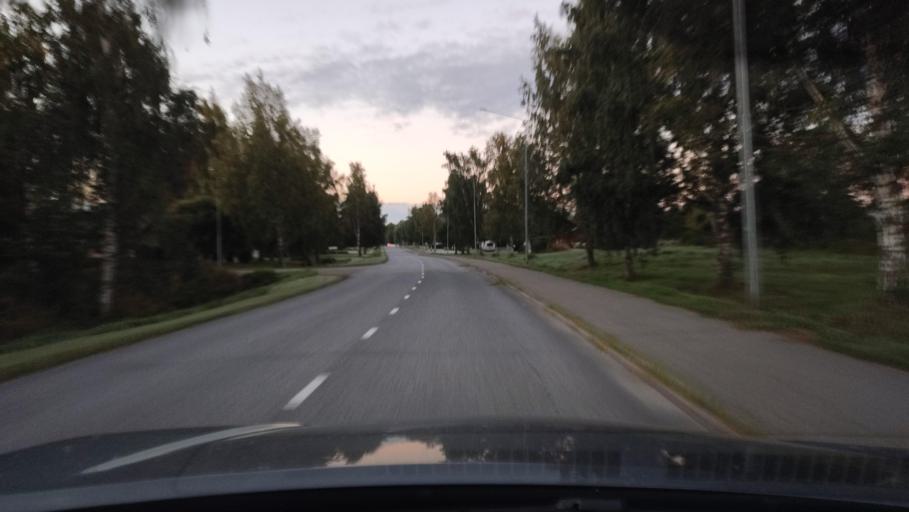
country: FI
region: Ostrobothnia
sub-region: Sydosterbotten
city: Kristinestad
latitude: 62.2799
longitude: 21.3636
